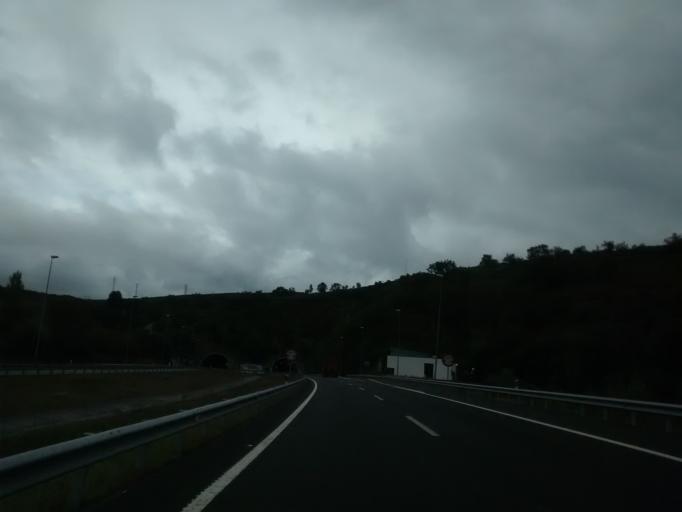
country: ES
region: Cantabria
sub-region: Provincia de Cantabria
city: Arenas de Iguna
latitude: 43.2010
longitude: -4.0721
